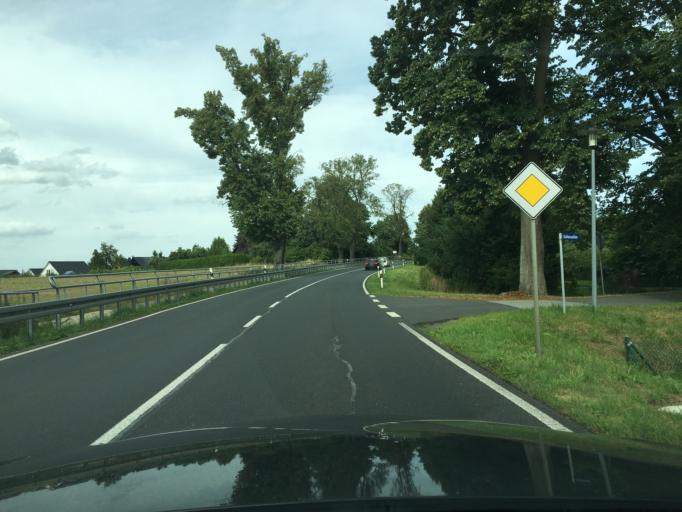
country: DE
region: Mecklenburg-Vorpommern
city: Neustrelitz
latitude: 53.3989
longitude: 13.1036
